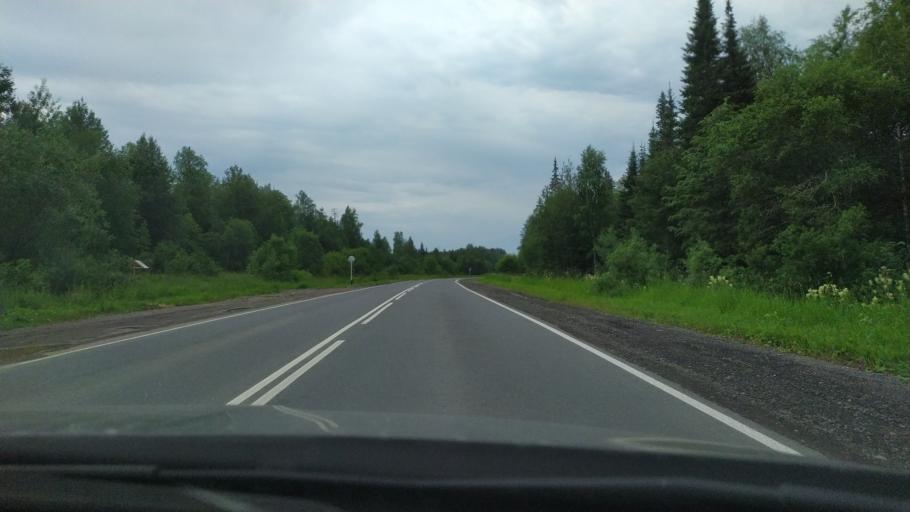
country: RU
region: Perm
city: Gremyachinsk
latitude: 58.4261
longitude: 57.8822
